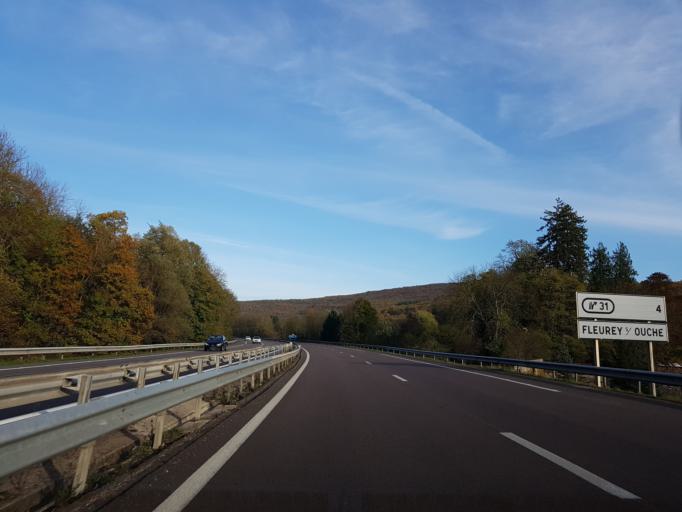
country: FR
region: Bourgogne
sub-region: Departement de la Cote-d'Or
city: Fleurey-sur-Ouche
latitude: 47.2976
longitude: 4.8095
